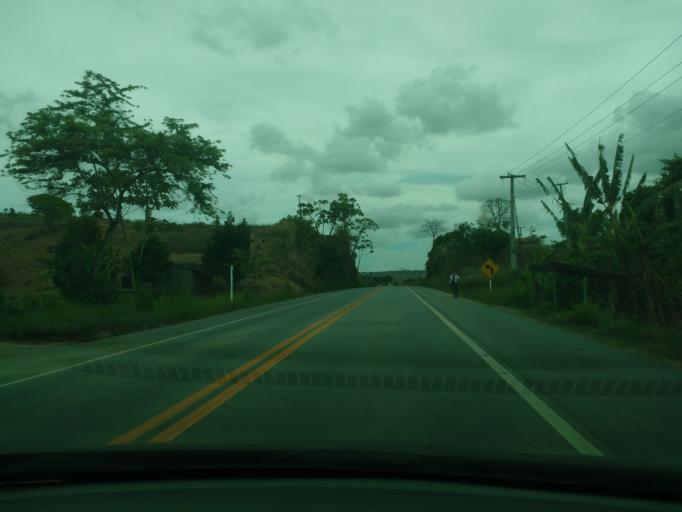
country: BR
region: Alagoas
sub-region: Murici
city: Murici
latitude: -9.2850
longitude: -35.9624
